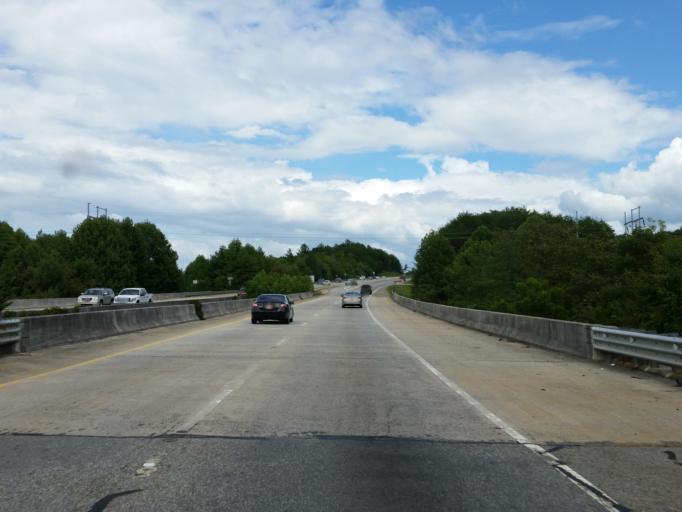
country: US
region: Georgia
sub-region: Fannin County
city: Blue Ridge
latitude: 34.8886
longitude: -84.2876
